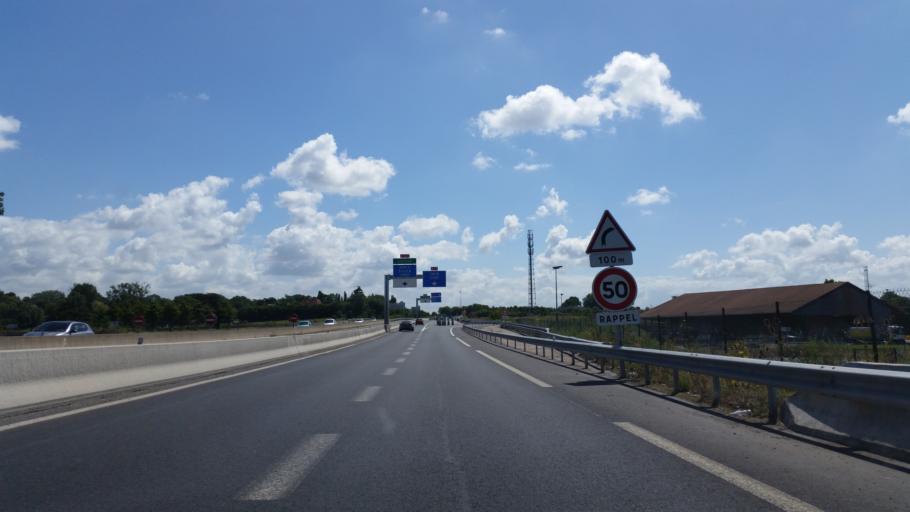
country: FR
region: Lower Normandy
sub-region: Departement du Calvados
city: Saint-Gatien-des-Bois
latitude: 49.2930
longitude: 0.1995
